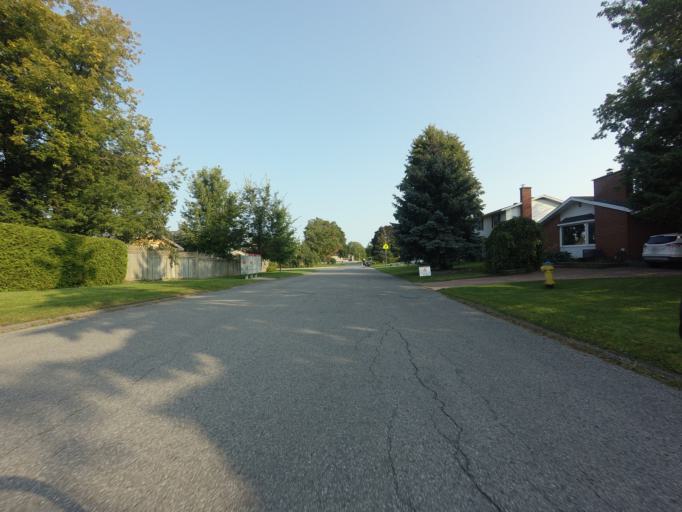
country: CA
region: Ontario
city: Bells Corners
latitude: 45.2973
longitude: -75.8869
